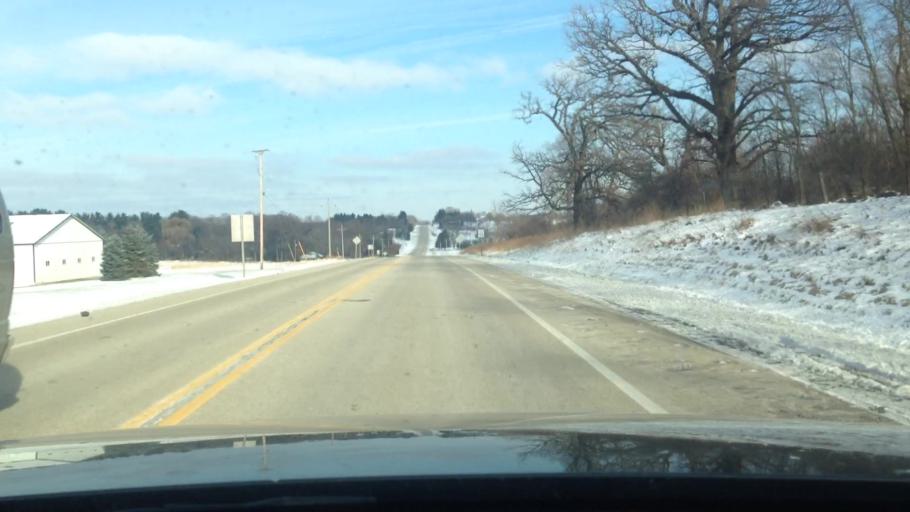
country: US
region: Wisconsin
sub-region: Walworth County
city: East Troy
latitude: 42.7466
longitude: -88.4061
